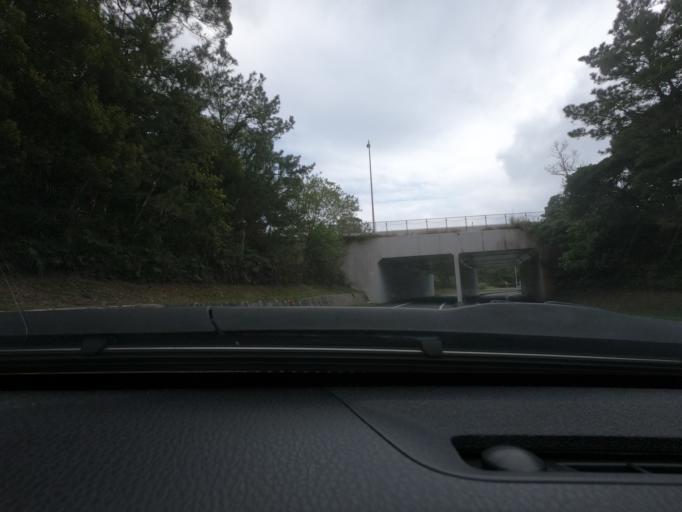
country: JP
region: Okinawa
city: Ishikawa
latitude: 26.4587
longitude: 127.9020
